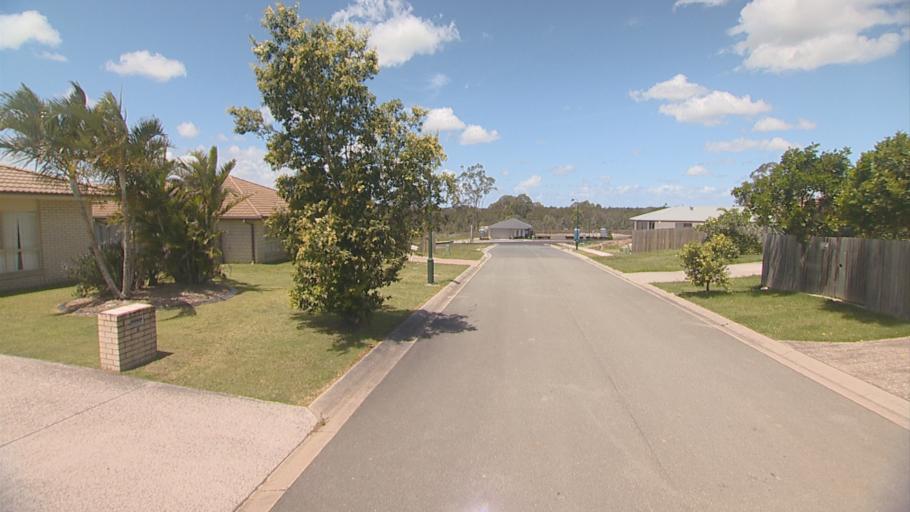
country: AU
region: Queensland
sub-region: Gold Coast
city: Yatala
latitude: -27.6948
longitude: 153.2213
